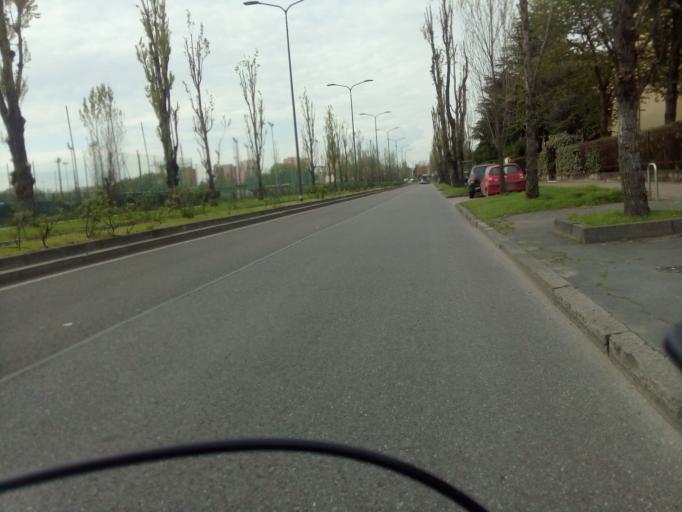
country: IT
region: Lombardy
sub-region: Citta metropolitana di Milano
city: Romano Banco
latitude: 45.4642
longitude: 9.1139
